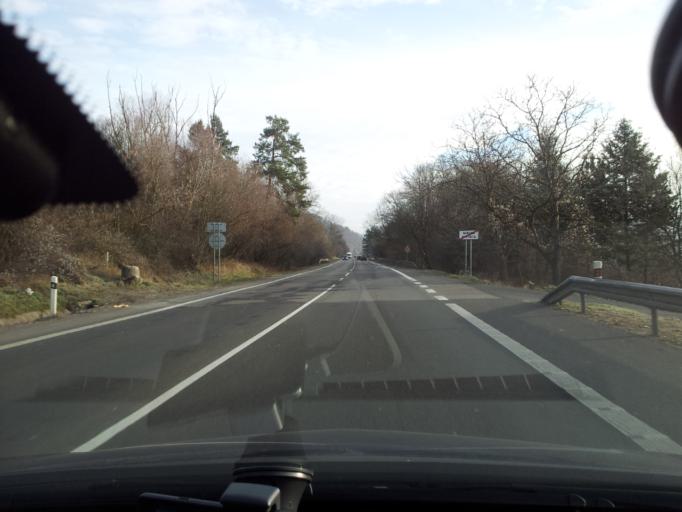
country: SK
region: Banskobystricky
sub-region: Okres Banska Bystrica
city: Banska Bystrica
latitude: 48.7422
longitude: 19.2061
